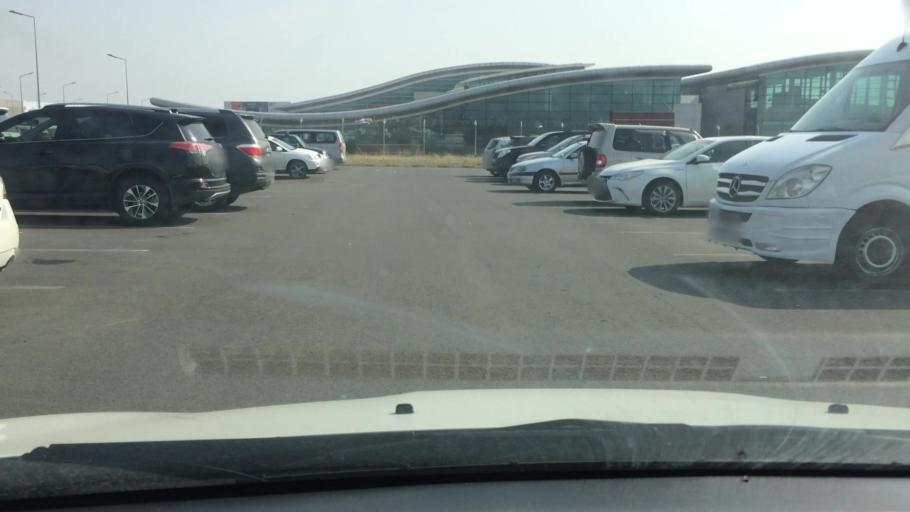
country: GE
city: Didi Lilo
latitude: 41.6713
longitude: 44.9624
